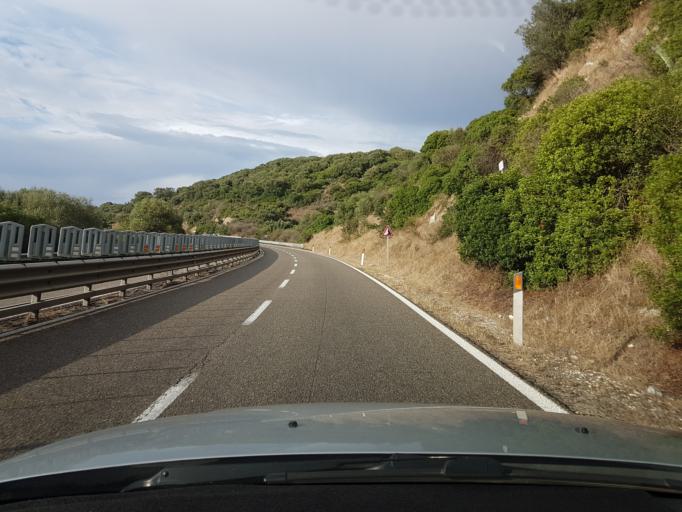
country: IT
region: Sardinia
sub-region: Provincia di Oristano
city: Bauladu
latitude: 40.0444
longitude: 8.7089
